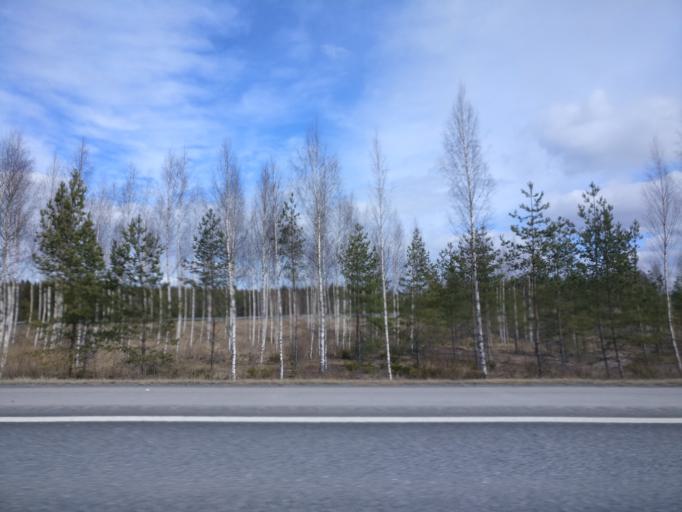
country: FI
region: Haeme
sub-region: Haemeenlinna
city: Janakkala
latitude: 60.9127
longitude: 24.5419
